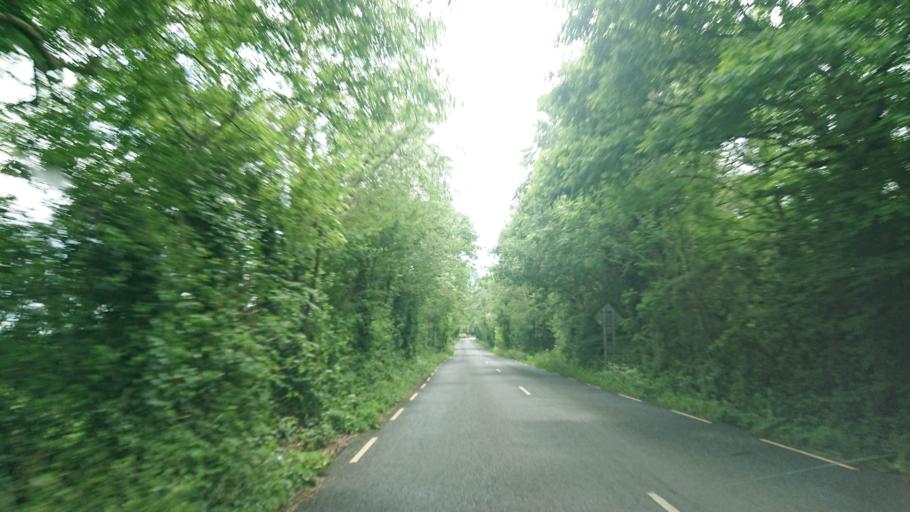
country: IE
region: Leinster
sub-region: Kilkenny
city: Graiguenamanagh
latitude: 52.5078
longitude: -6.9463
